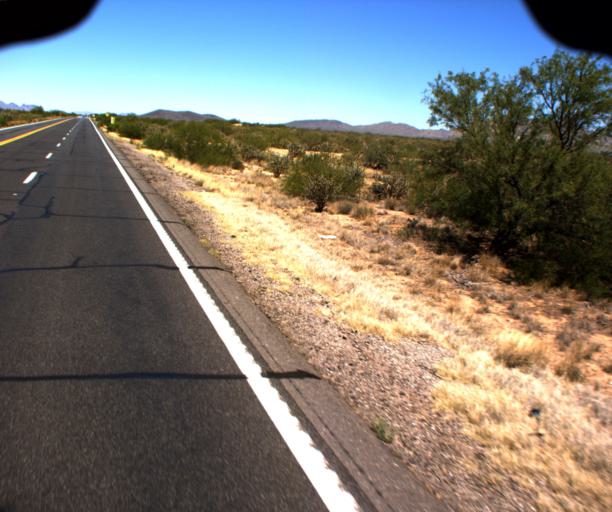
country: US
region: Arizona
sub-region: Yavapai County
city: Congress
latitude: 34.1357
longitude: -112.9681
